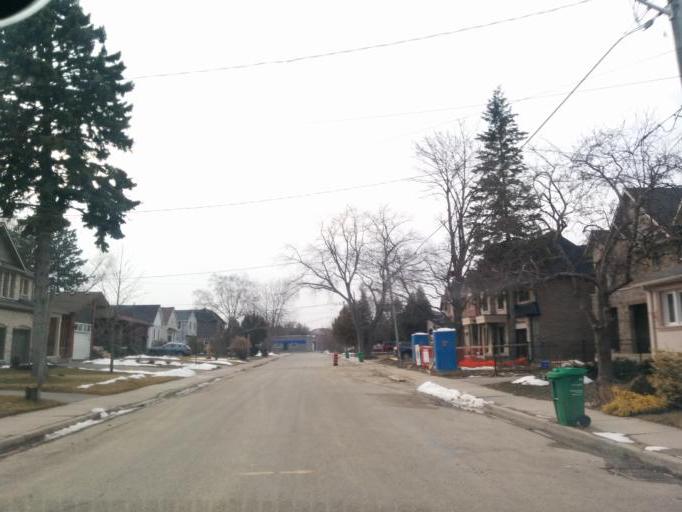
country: CA
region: Ontario
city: Mississauga
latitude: 43.5460
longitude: -79.5948
